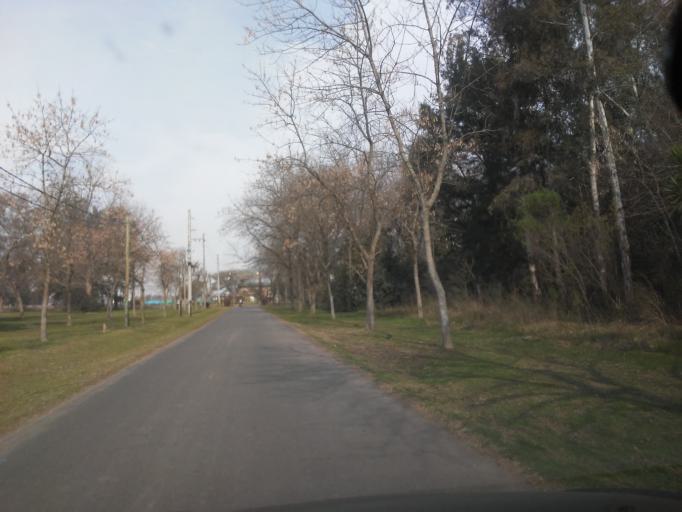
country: AR
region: Buenos Aires
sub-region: Partido de Marcos Paz
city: Marcos Paz
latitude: -34.6694
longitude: -58.8569
